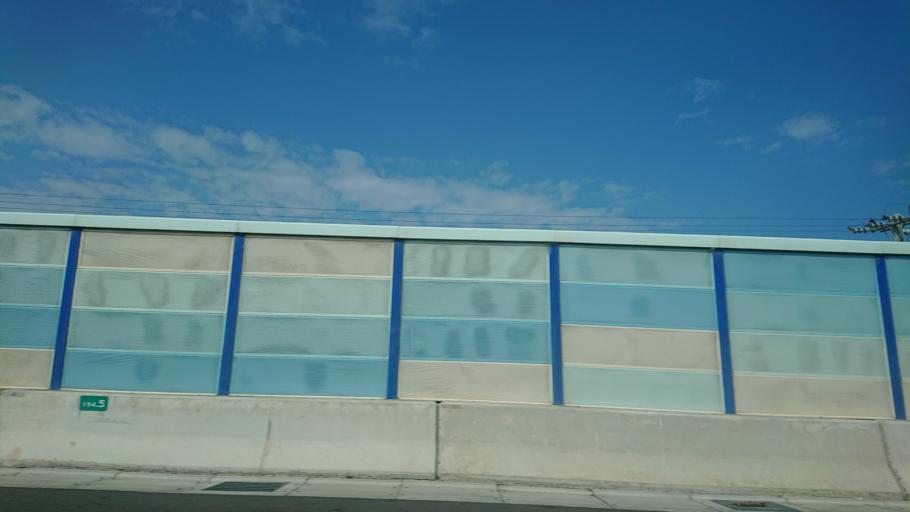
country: TW
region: Taiwan
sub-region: Changhua
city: Chang-hua
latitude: 23.9589
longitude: 120.3345
